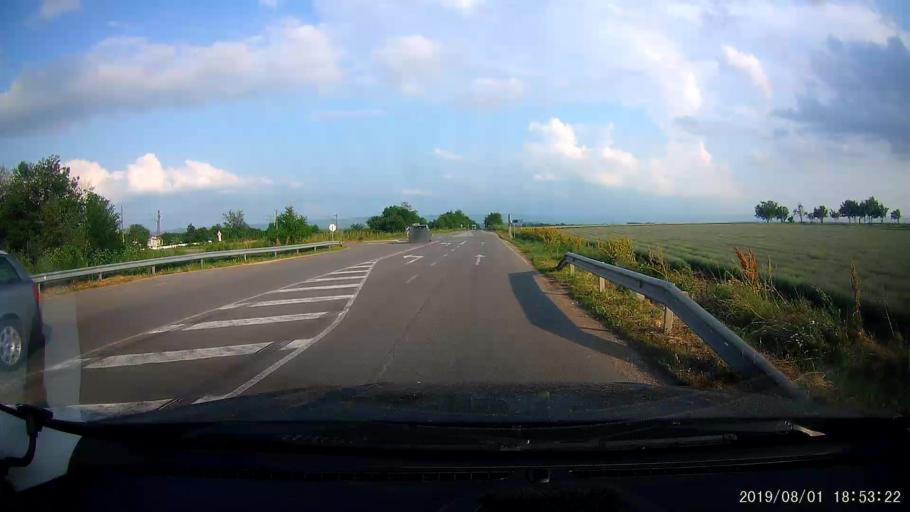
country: BG
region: Shumen
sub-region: Obshtina Shumen
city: Shumen
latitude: 43.2222
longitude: 26.9927
